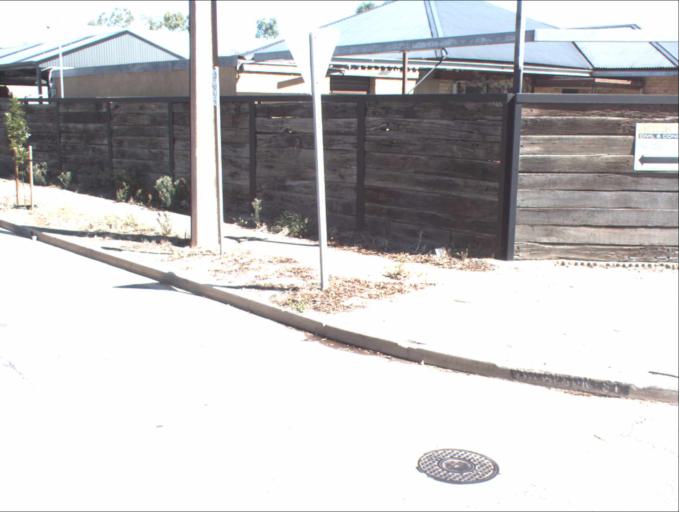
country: AU
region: South Australia
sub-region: Port Adelaide Enfield
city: Enfield
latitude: -34.8349
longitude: 138.5902
